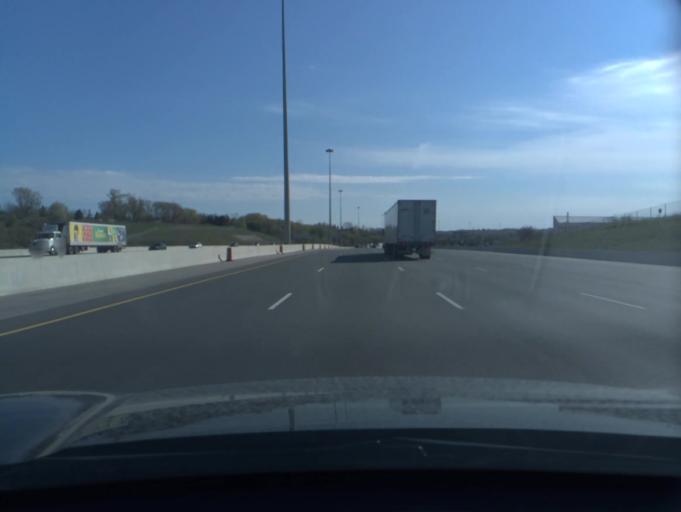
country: CA
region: Ontario
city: North Perth
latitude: 43.8181
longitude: -80.9998
